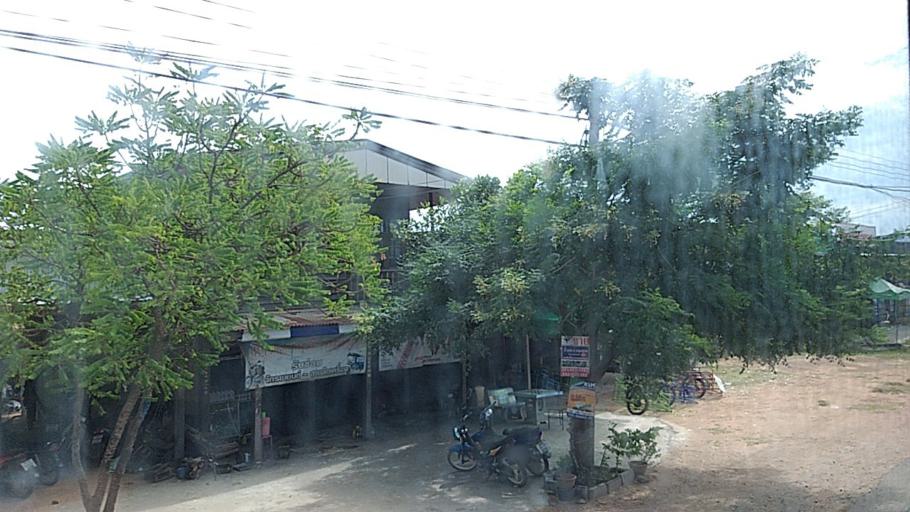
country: TH
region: Maha Sarakham
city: Chiang Yuen
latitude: 16.3994
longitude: 103.1000
